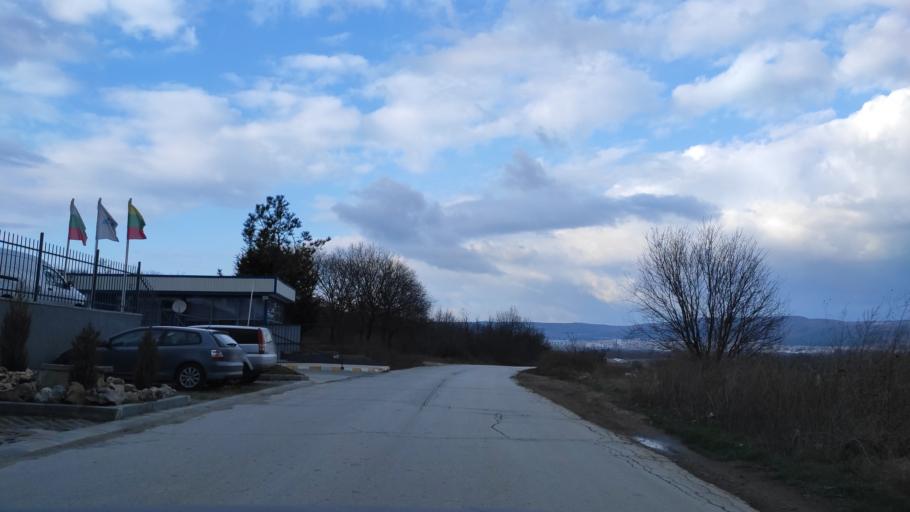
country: BG
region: Varna
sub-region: Obshtina Aksakovo
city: Aksakovo
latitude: 43.2264
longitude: 27.8049
